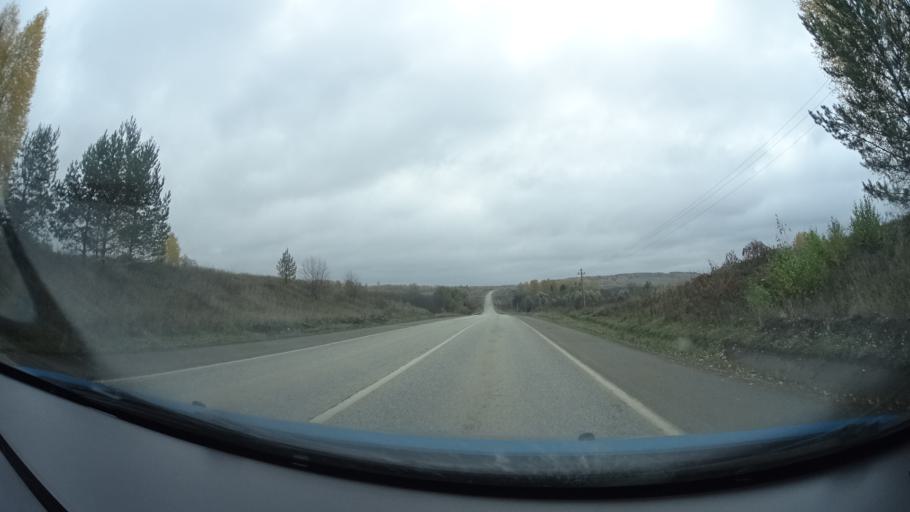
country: RU
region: Perm
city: Osa
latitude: 57.1512
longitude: 55.5293
